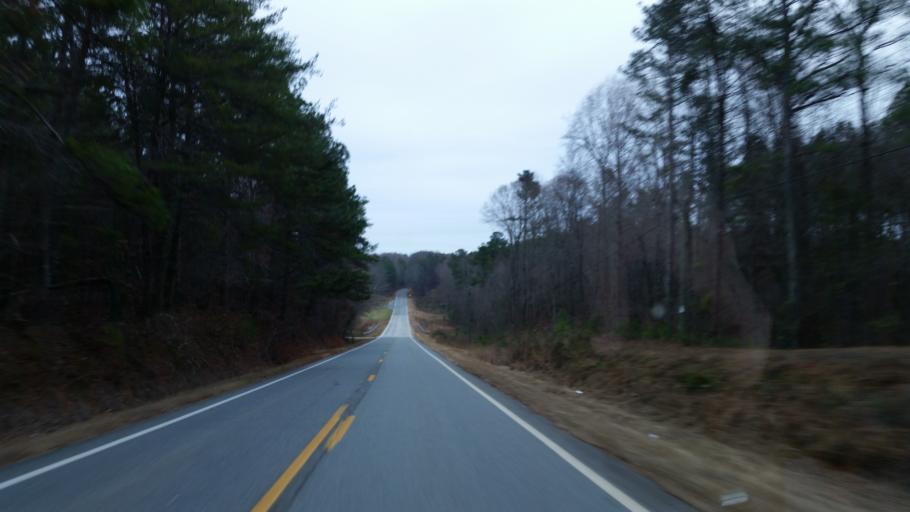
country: US
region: Georgia
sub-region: Dawson County
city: Dawsonville
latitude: 34.4465
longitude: -84.1127
